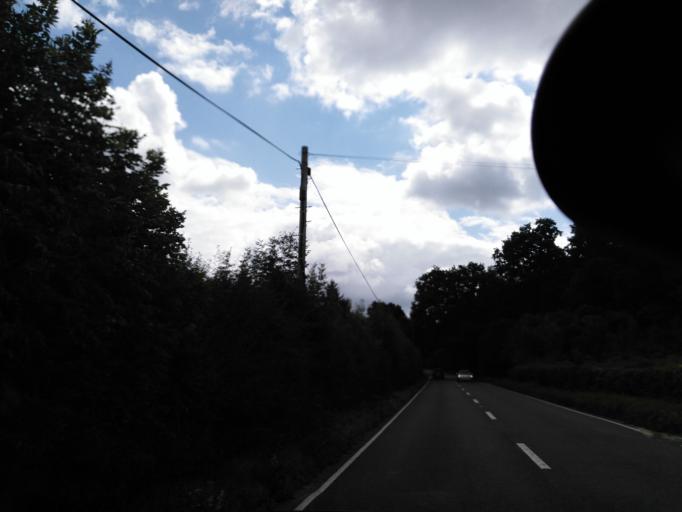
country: GB
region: England
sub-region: Dorset
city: Lytchett Matravers
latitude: 50.7769
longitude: -2.0702
